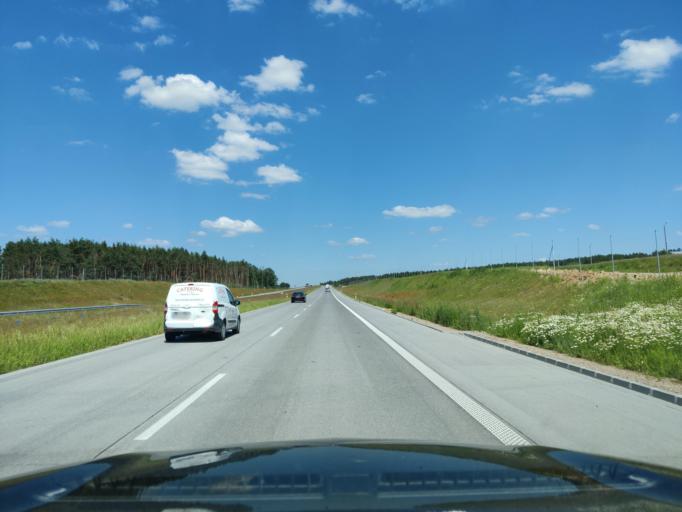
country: PL
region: Masovian Voivodeship
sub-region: Powiat mlawski
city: Strzegowo
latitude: 52.9743
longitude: 20.3276
